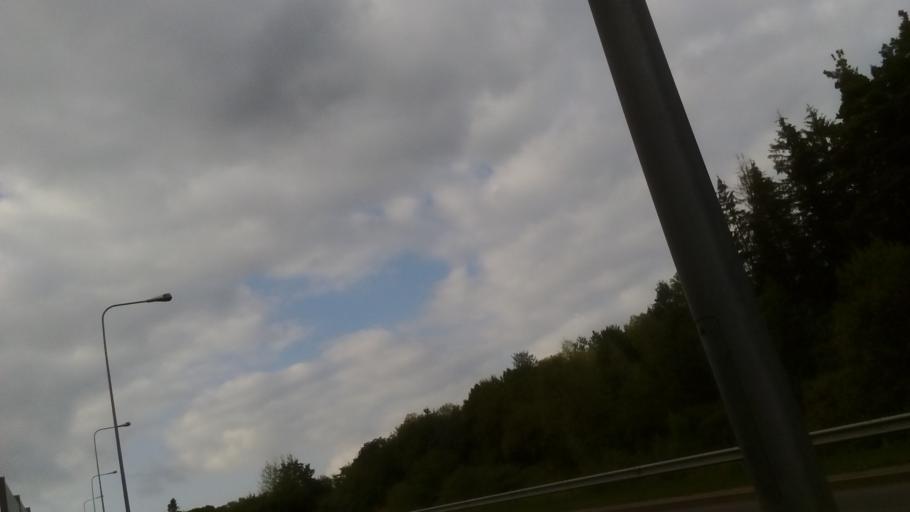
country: LT
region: Alytaus apskritis
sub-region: Alytus
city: Alytus
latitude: 54.4230
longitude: 24.0357
